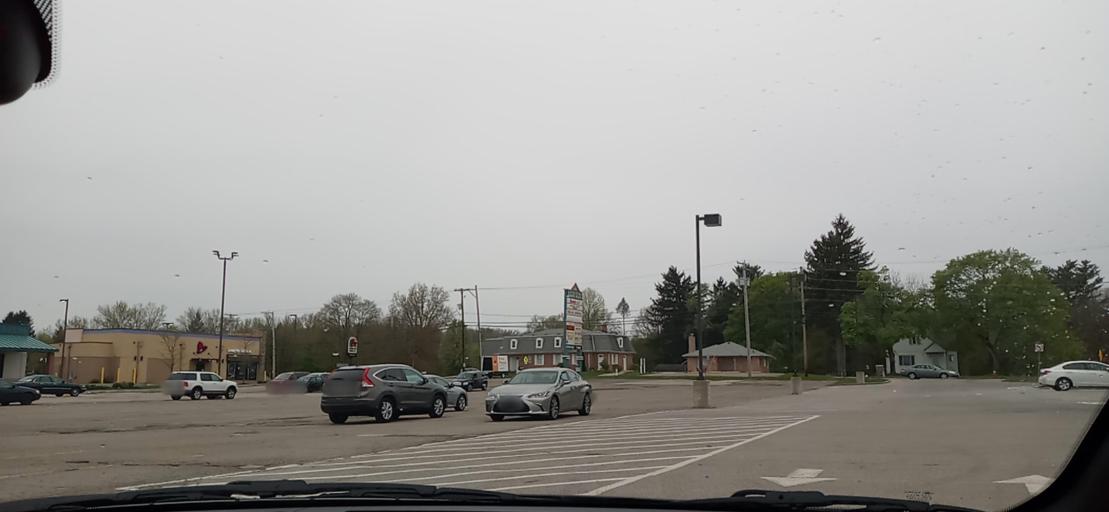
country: US
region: Ohio
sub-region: Summit County
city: Portage Lakes
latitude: 41.0098
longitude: -81.5538
